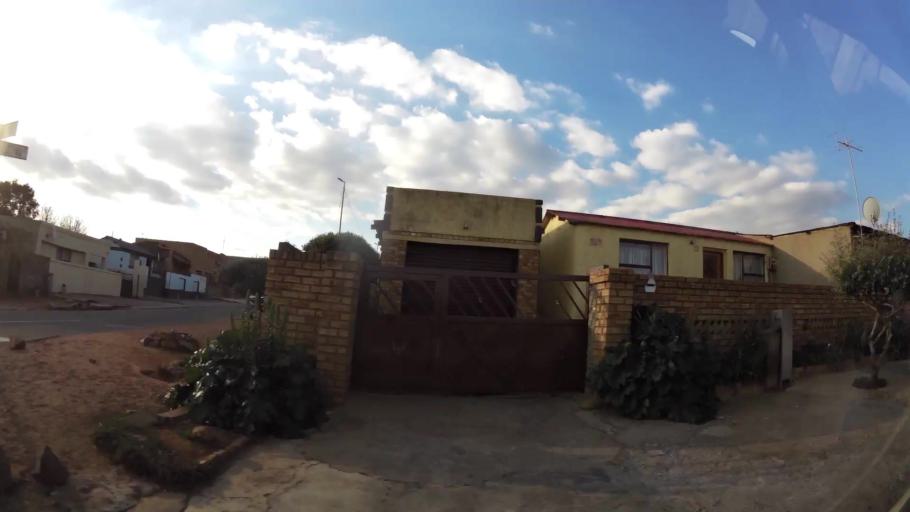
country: ZA
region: Gauteng
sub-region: West Rand District Municipality
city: Krugersdorp
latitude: -26.0739
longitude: 27.7566
